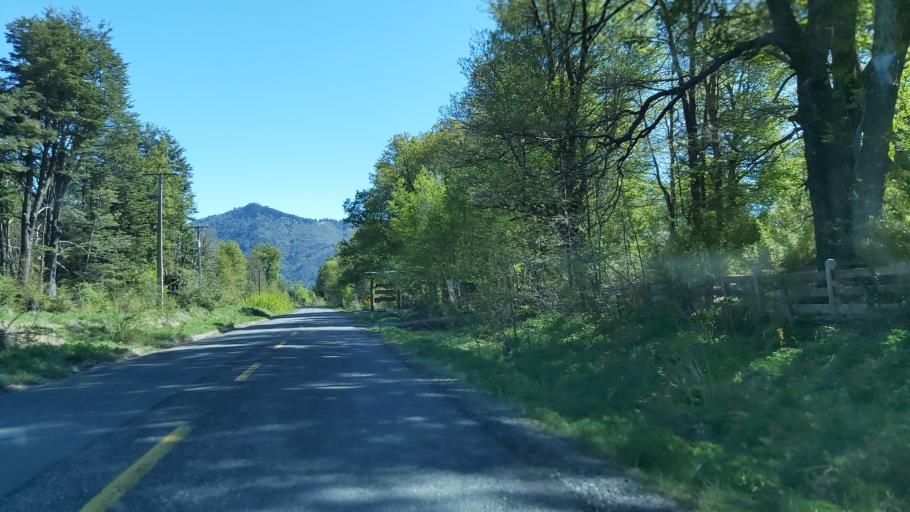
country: CL
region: Araucania
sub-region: Provincia de Cautin
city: Vilcun
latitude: -38.4713
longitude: -71.5255
